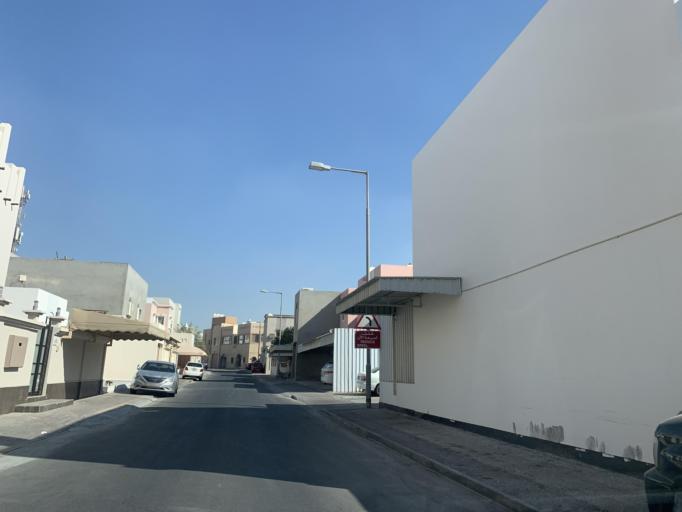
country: BH
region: Central Governorate
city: Madinat Hamad
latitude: 26.1172
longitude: 50.5057
